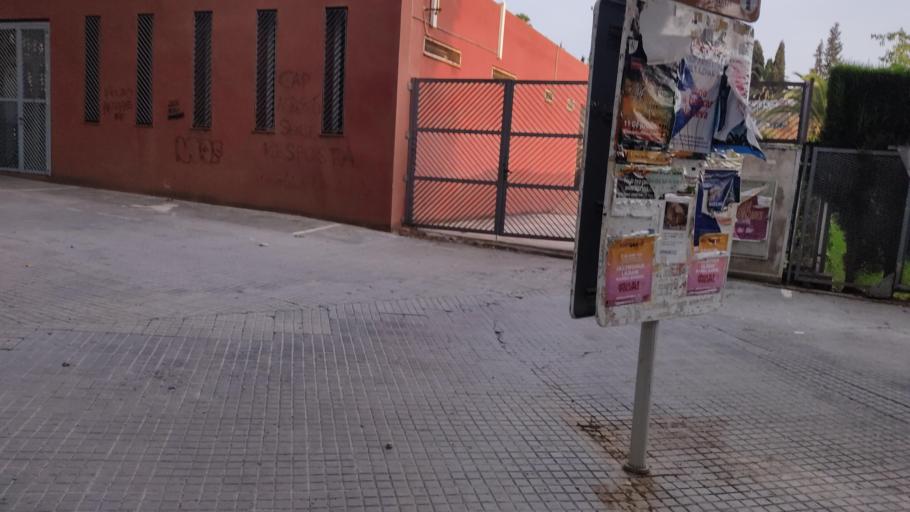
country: ES
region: Catalonia
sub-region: Provincia de Barcelona
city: Molins de Rei
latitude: 41.4123
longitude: 2.0215
